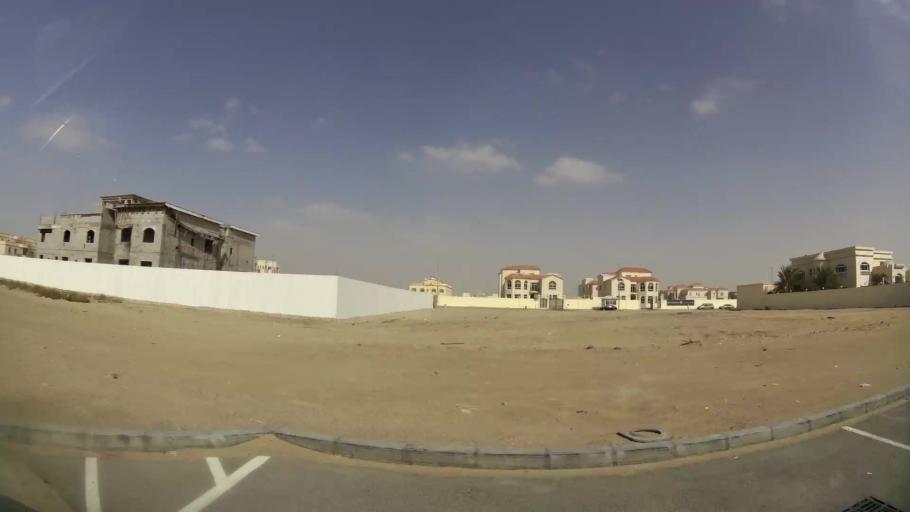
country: AE
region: Abu Dhabi
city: Abu Dhabi
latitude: 24.4329
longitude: 54.5851
